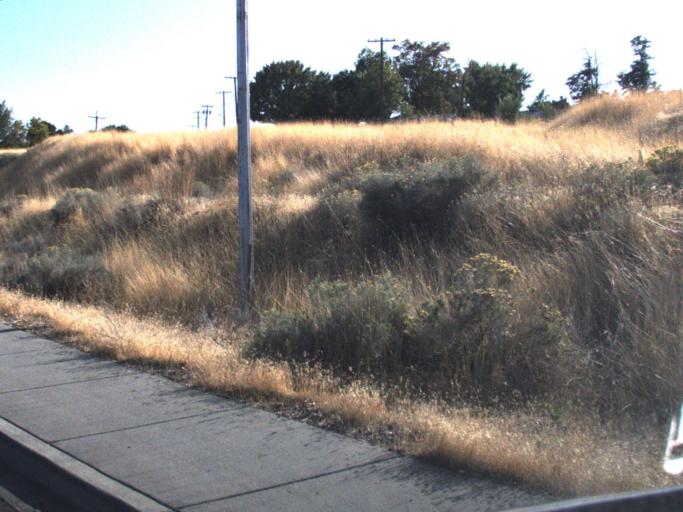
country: US
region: Washington
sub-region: Franklin County
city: Pasco
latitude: 46.2017
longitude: -119.0965
